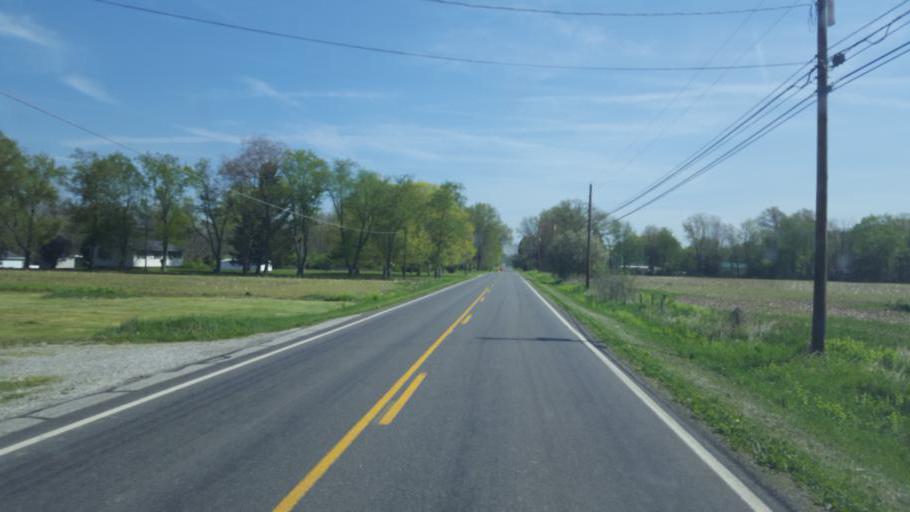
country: US
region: Ohio
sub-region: Medina County
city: Lodi
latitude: 41.0150
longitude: -82.0476
